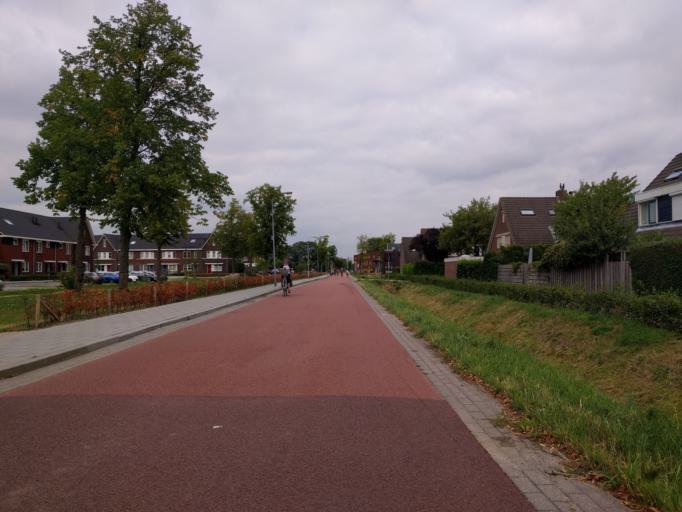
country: NL
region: Gelderland
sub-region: Gemeente Nijmegen
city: Nijmegen
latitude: 51.8680
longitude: 5.8665
